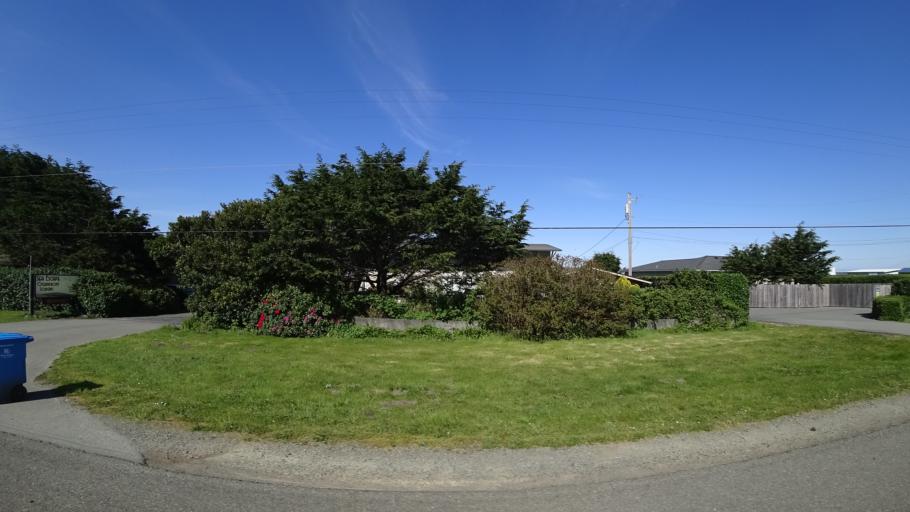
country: US
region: Oregon
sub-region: Curry County
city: Harbor
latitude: 41.9760
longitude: -124.2030
